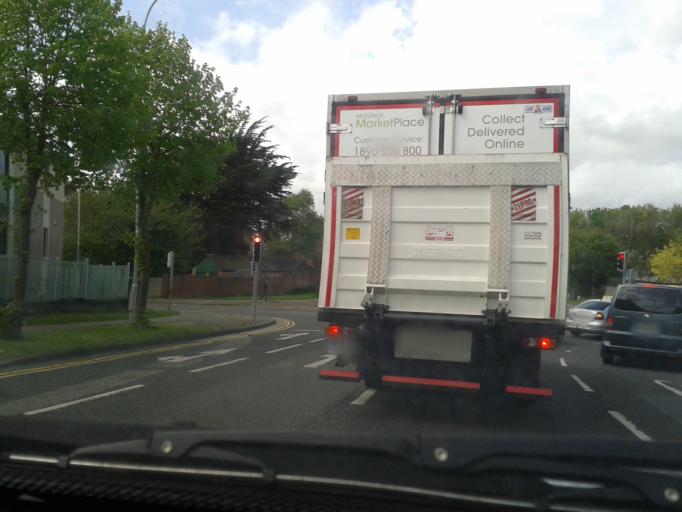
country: IE
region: Leinster
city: Glasnevin
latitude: 53.3788
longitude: -6.2663
